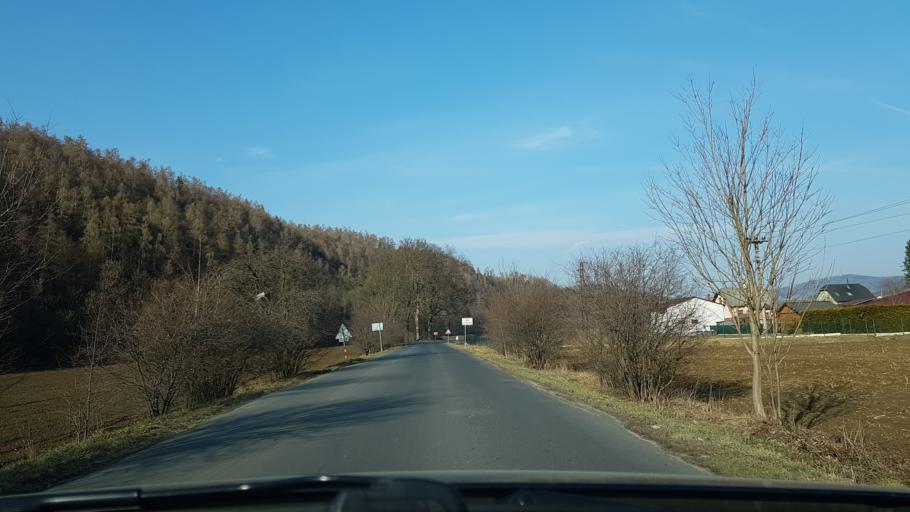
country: CZ
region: Olomoucky
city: Olsany
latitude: 49.9736
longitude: 16.8660
